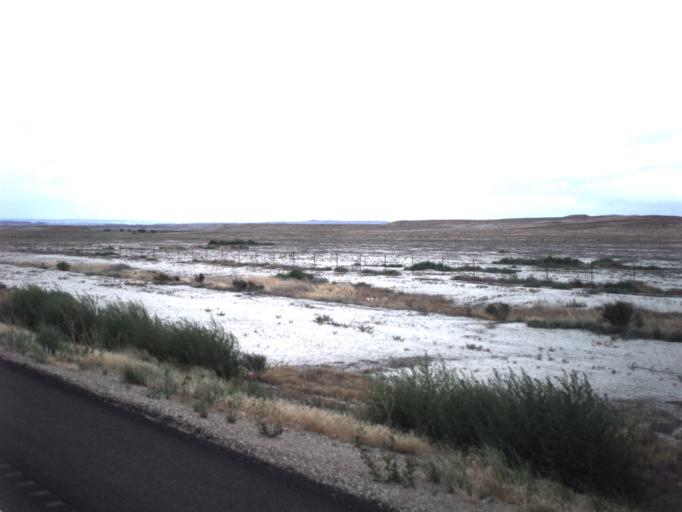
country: US
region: Utah
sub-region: Carbon County
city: East Carbon City
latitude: 38.9955
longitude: -110.2583
